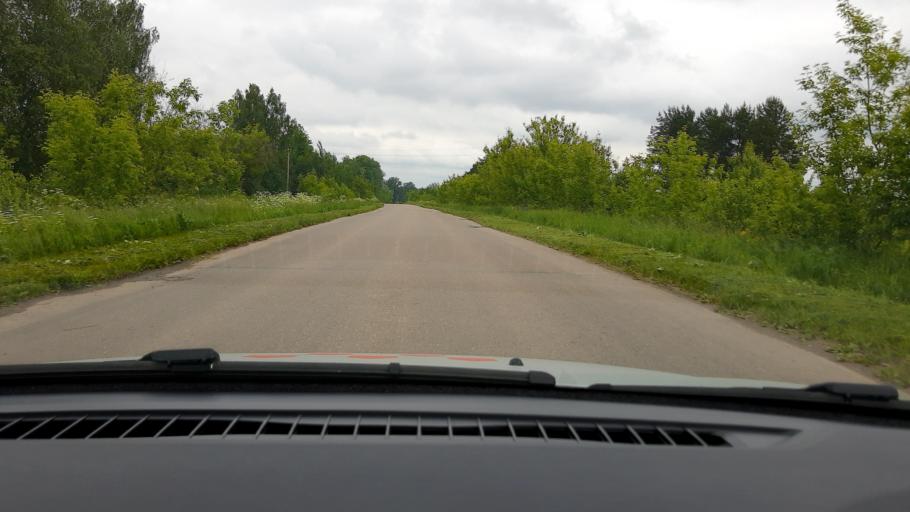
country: RU
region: Nizjnij Novgorod
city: Bogorodsk
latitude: 56.0665
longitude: 43.5022
